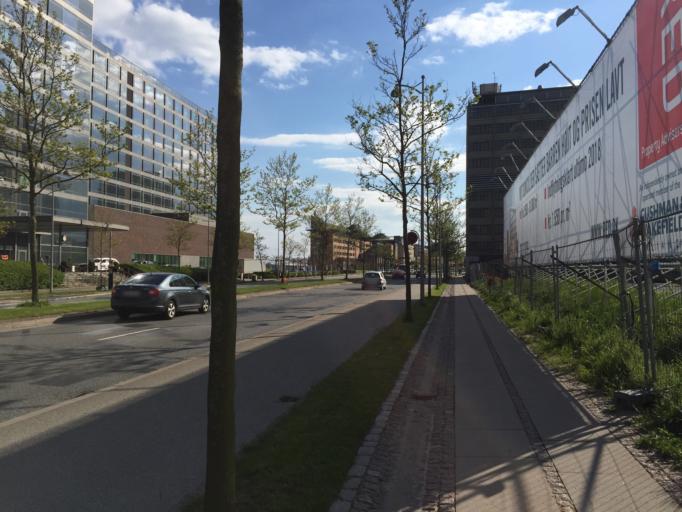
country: DK
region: Capital Region
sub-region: Kobenhavn
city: Copenhagen
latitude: 55.6695
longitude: 12.5741
